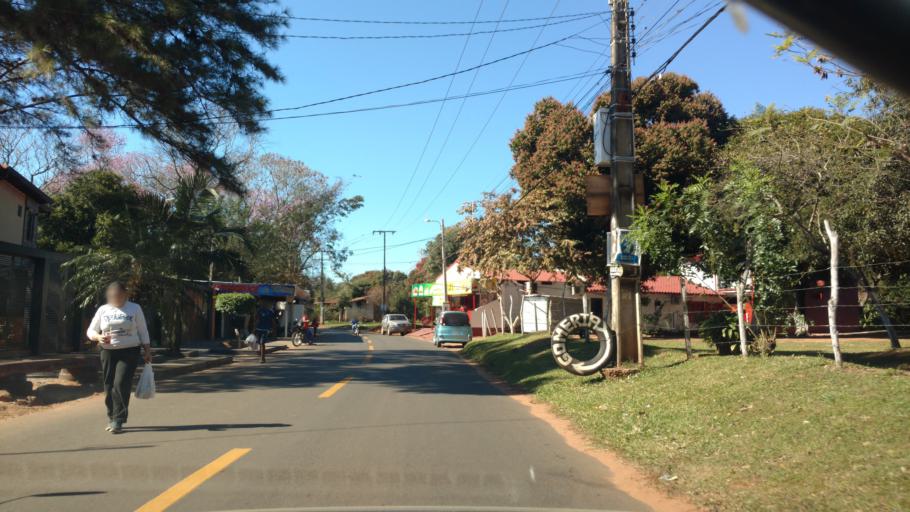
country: PY
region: Central
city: Capiata
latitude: -25.3620
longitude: -57.4143
